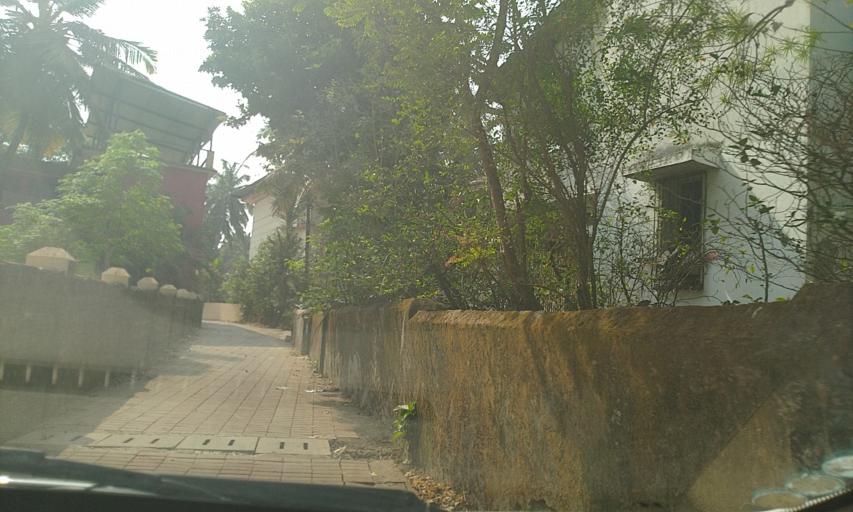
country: IN
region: Goa
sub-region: North Goa
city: Taleigao
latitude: 15.4660
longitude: 73.8200
